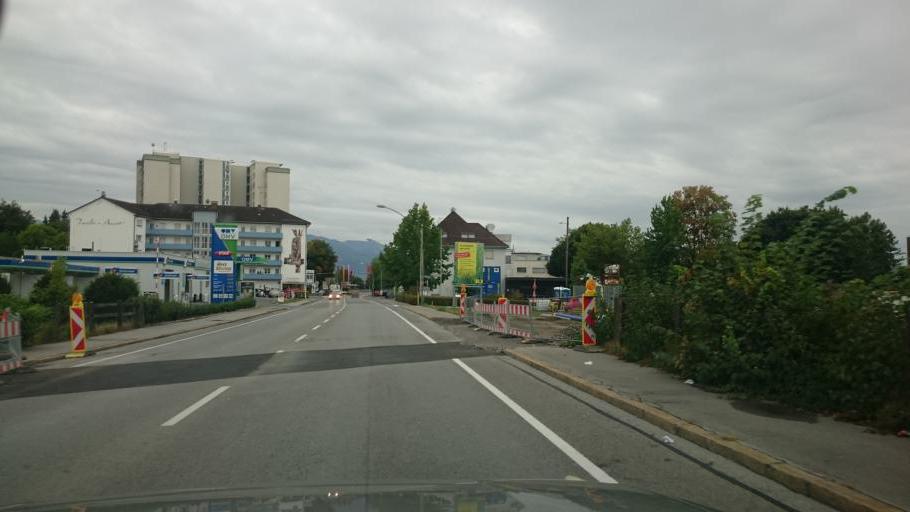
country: AT
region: Vorarlberg
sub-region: Politischer Bezirk Bregenz
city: Lauterach
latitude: 47.4886
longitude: 9.7330
